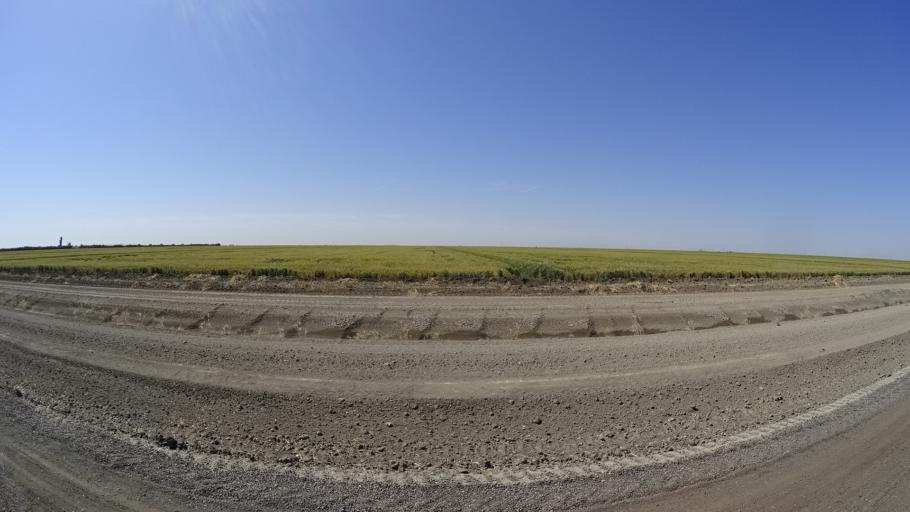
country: US
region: California
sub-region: Kings County
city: Corcoran
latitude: 36.0072
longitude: -119.5585
